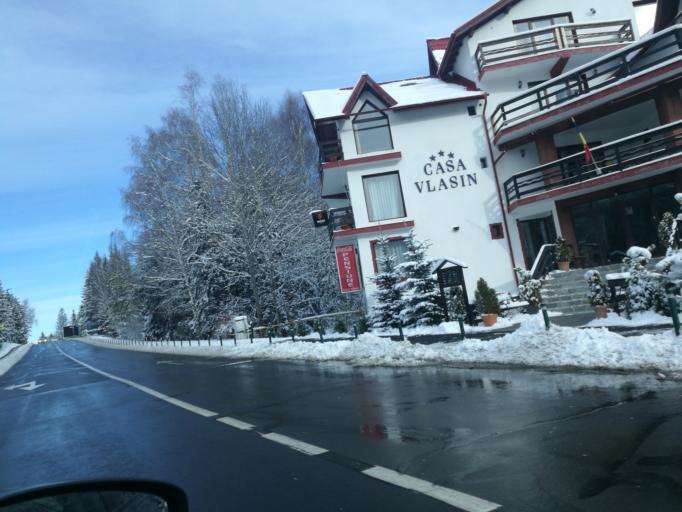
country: RO
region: Brasov
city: Brasov
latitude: 45.5961
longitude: 25.5531
